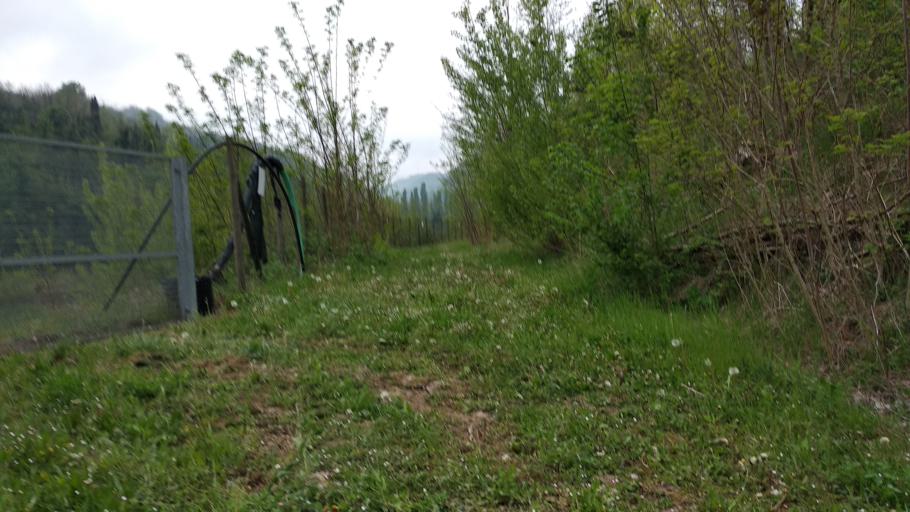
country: IT
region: Emilia-Romagna
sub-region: Forli-Cesena
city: Modigliana
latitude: 44.1407
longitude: 11.8012
